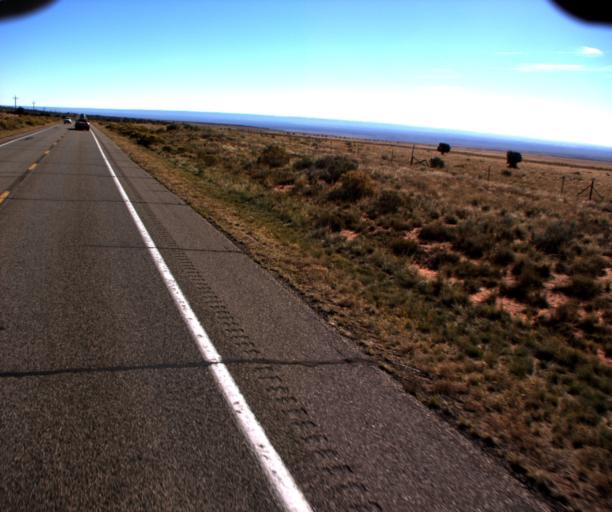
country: US
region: Arizona
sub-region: Mohave County
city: Colorado City
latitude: 36.8583
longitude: -112.7970
